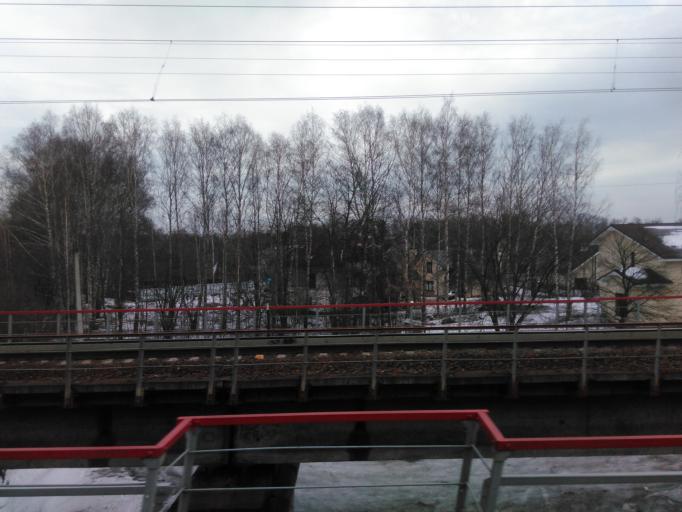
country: RU
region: Moskovskaya
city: Mamontovka
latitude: 55.9689
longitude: 37.8129
